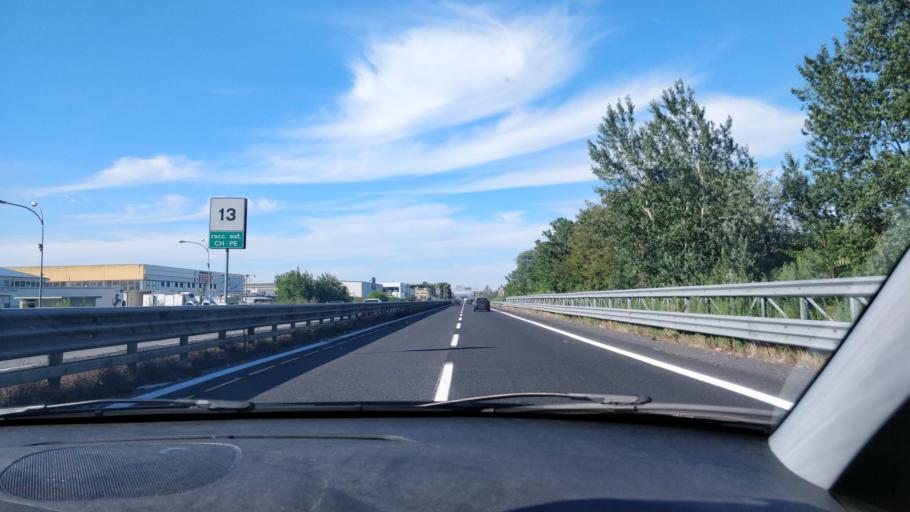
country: IT
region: Abruzzo
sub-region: Provincia di Chieti
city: Sambuceto
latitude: 42.4341
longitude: 14.1803
